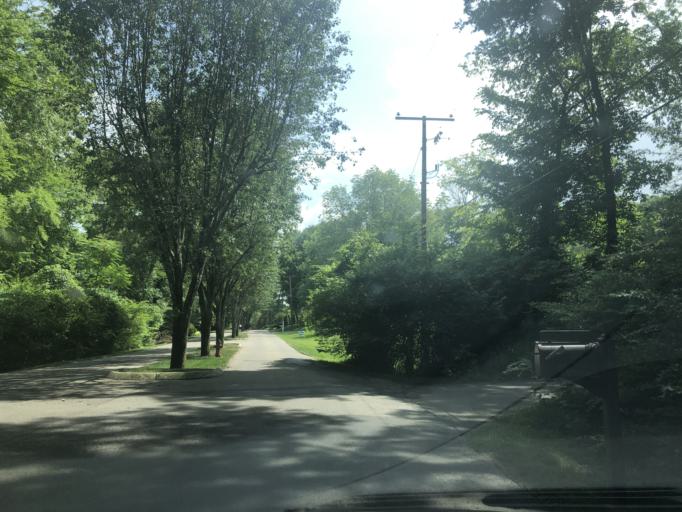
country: US
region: Tennessee
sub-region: Davidson County
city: Forest Hills
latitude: 36.0626
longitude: -86.8654
